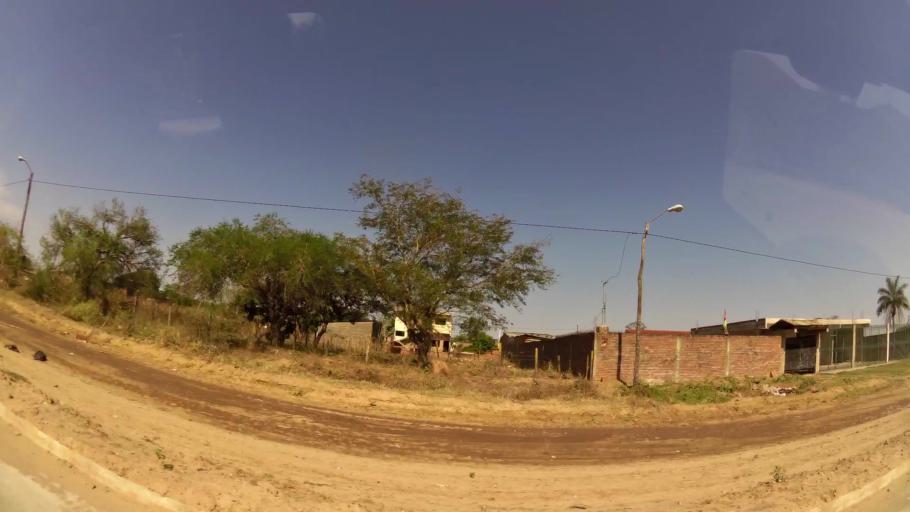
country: BO
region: Santa Cruz
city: Cotoca
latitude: -17.7146
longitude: -63.0684
